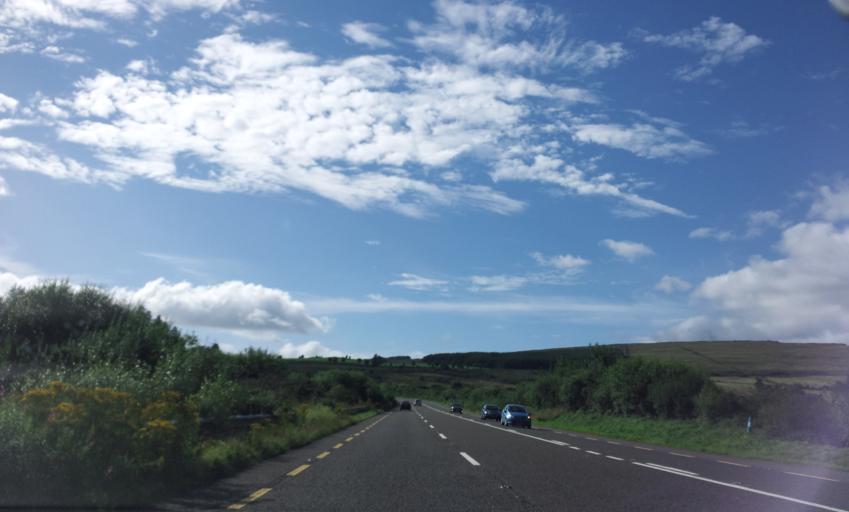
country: IE
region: Munster
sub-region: County Cork
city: Millstreet
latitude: 51.9610
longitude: -9.2030
